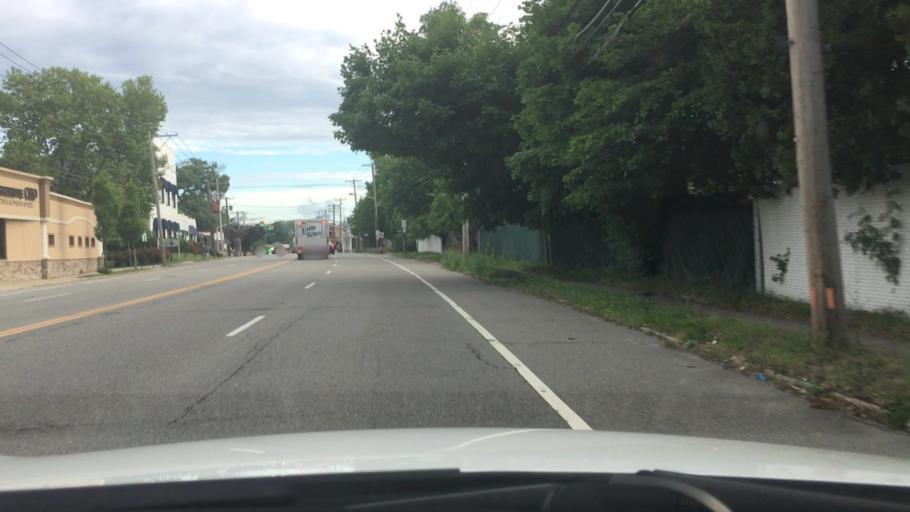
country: US
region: New York
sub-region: Nassau County
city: Albertson
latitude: 40.7736
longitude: -73.6493
